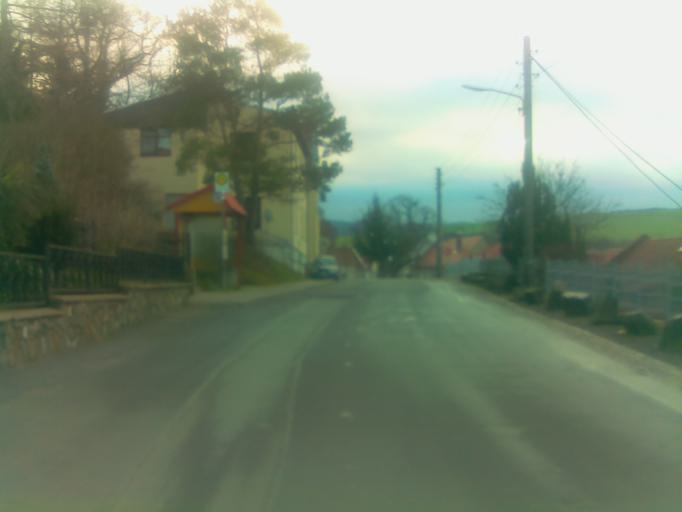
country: DE
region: Thuringia
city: Weira
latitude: 50.7274
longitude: 11.7143
